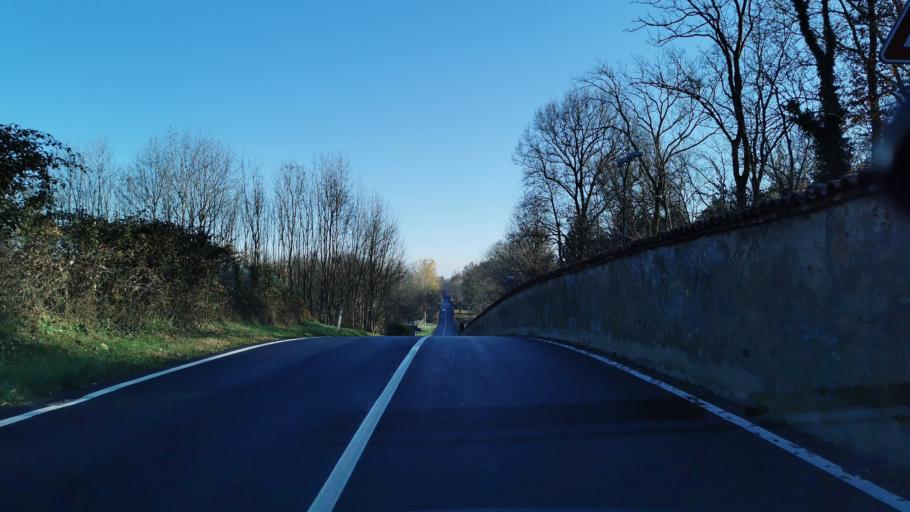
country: IT
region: Piedmont
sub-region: Provincia di Torino
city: Fiano
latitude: 45.2025
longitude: 7.5349
